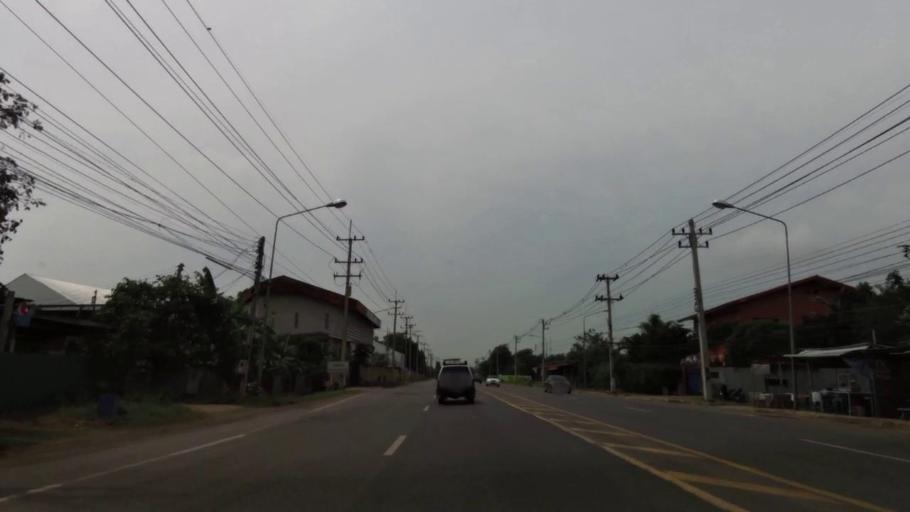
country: TH
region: Lop Buri
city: Ban Mi
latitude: 15.0519
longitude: 100.5764
